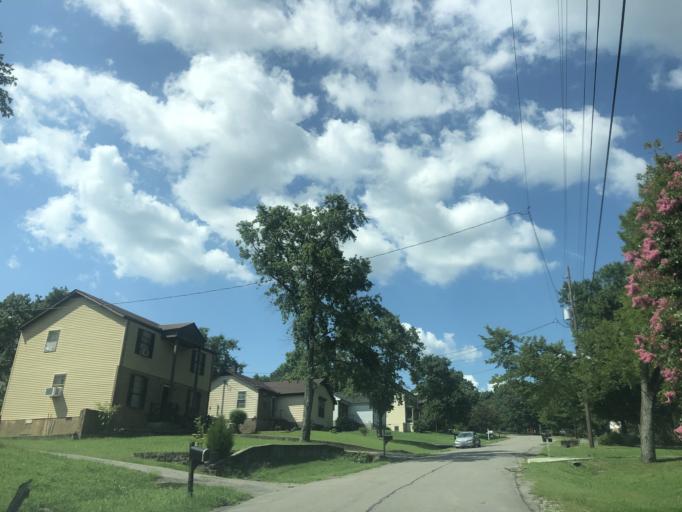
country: US
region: Tennessee
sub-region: Wilson County
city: Green Hill
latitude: 36.2071
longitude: -86.5861
